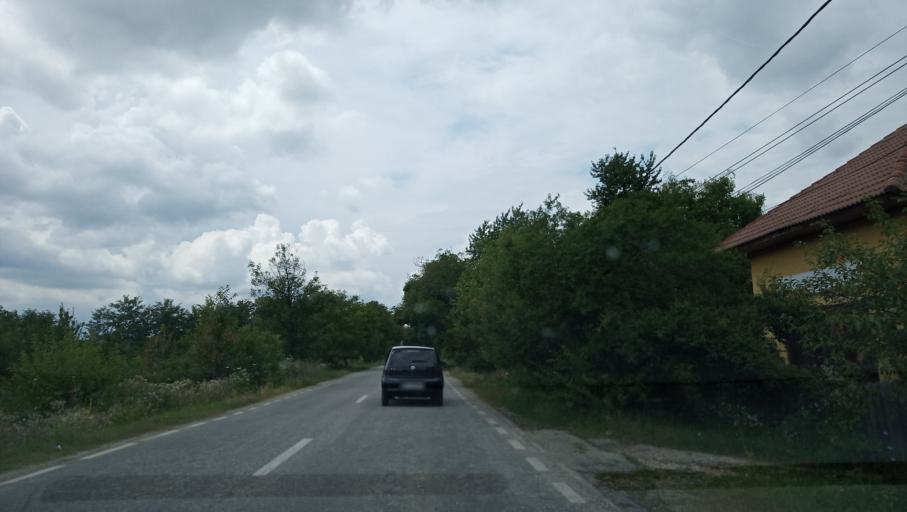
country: RO
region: Gorj
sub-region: Comuna Pestisani
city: Pestisani
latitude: 45.0823
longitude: 23.0602
